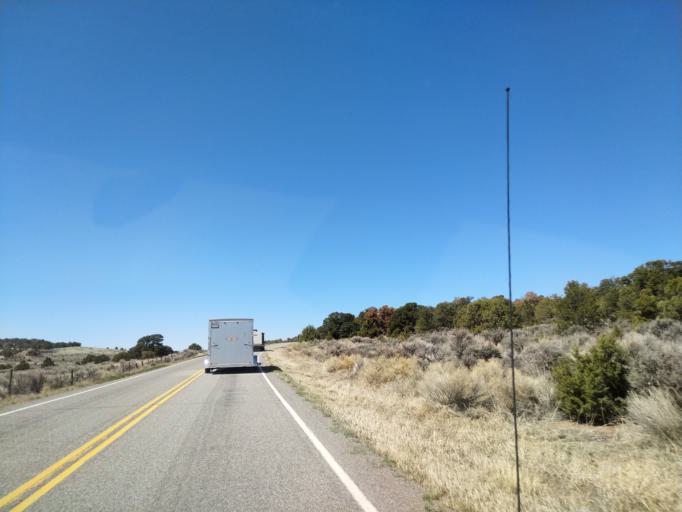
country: US
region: Colorado
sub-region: Mesa County
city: Redlands
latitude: 39.0048
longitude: -108.6978
